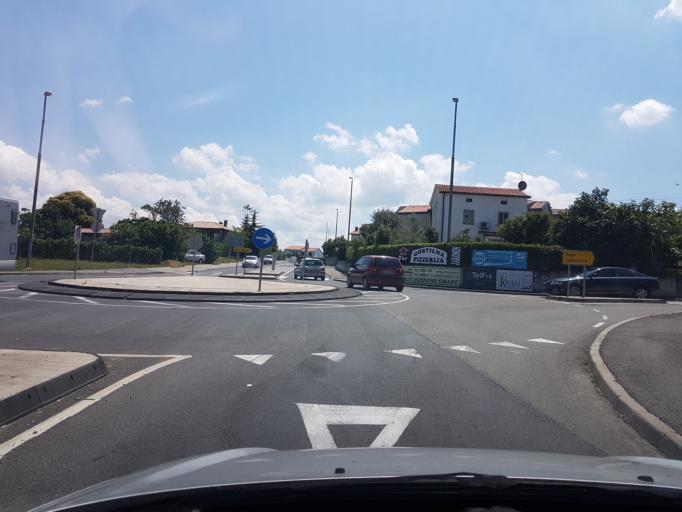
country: SI
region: Koper-Capodistria
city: Prade
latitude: 45.5443
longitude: 13.7658
